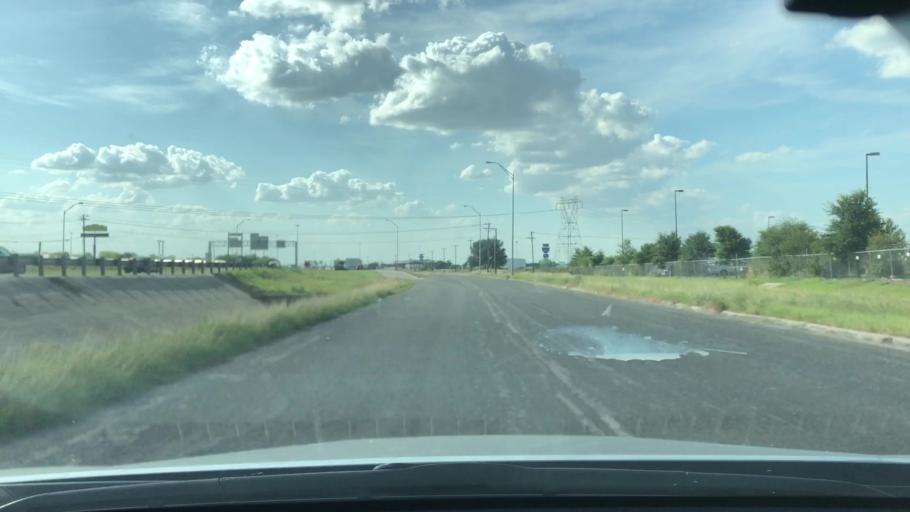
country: US
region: Texas
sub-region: Bexar County
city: Kirby
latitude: 29.4418
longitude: -98.3933
